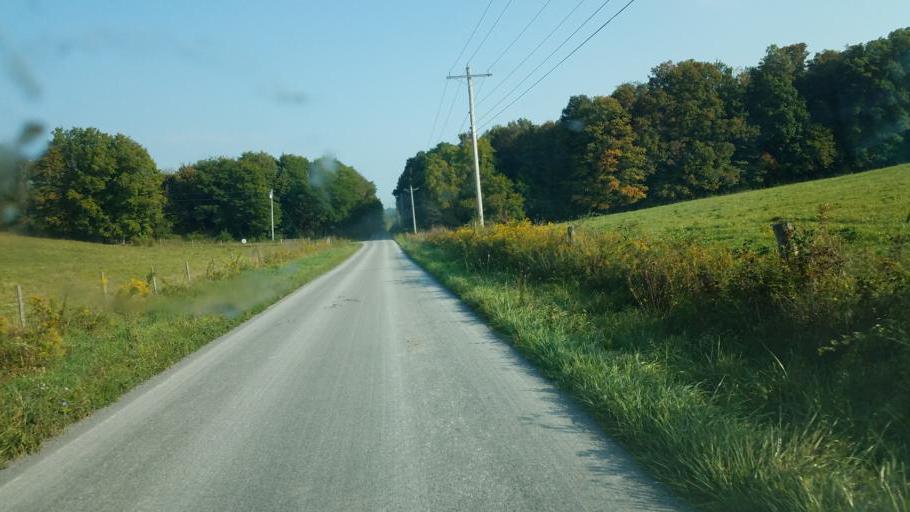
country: US
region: Ohio
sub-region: Knox County
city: Fredericktown
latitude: 40.5339
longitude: -82.6332
